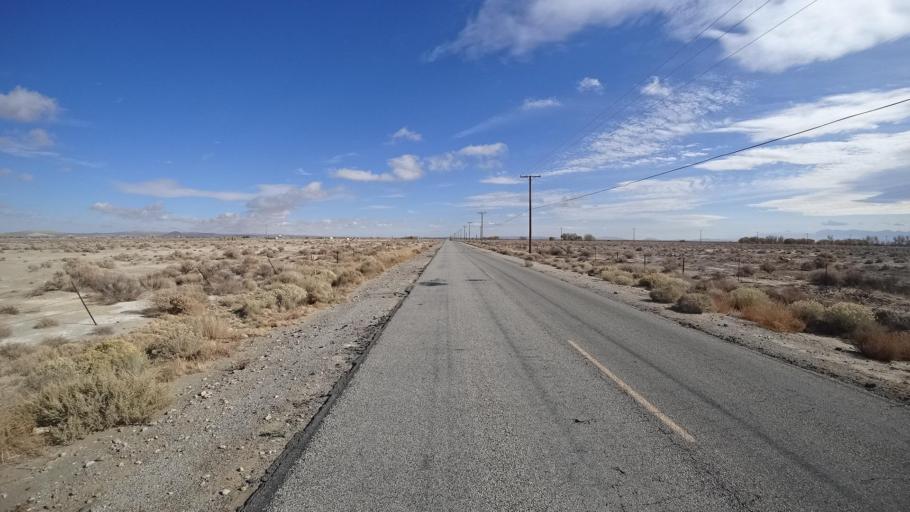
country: US
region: California
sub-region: Kern County
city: Rosamond
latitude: 34.8202
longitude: -118.1874
